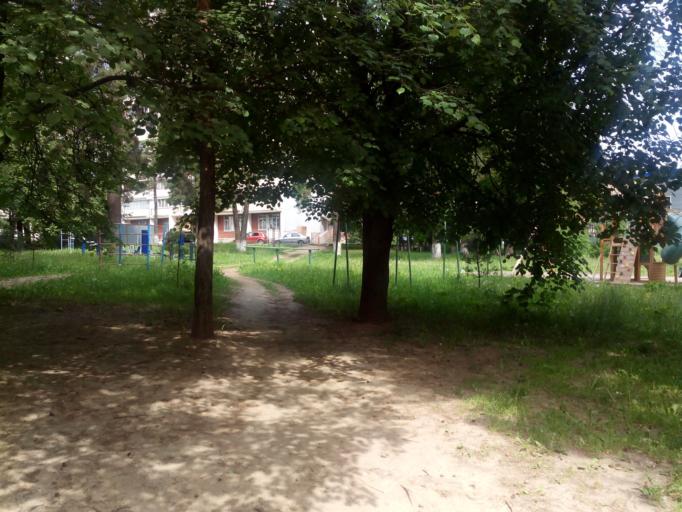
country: RU
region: Moskovskaya
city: Odintsovo
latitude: 55.6654
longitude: 37.2947
